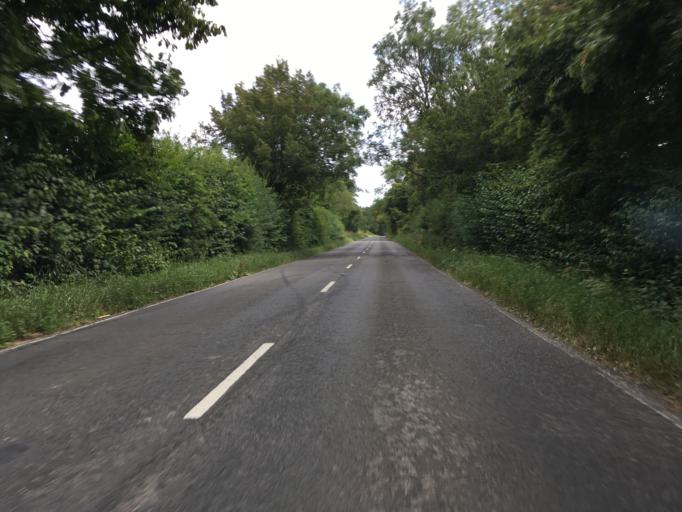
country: GB
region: England
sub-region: Kent
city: Tenterden
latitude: 51.0521
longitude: 0.7329
